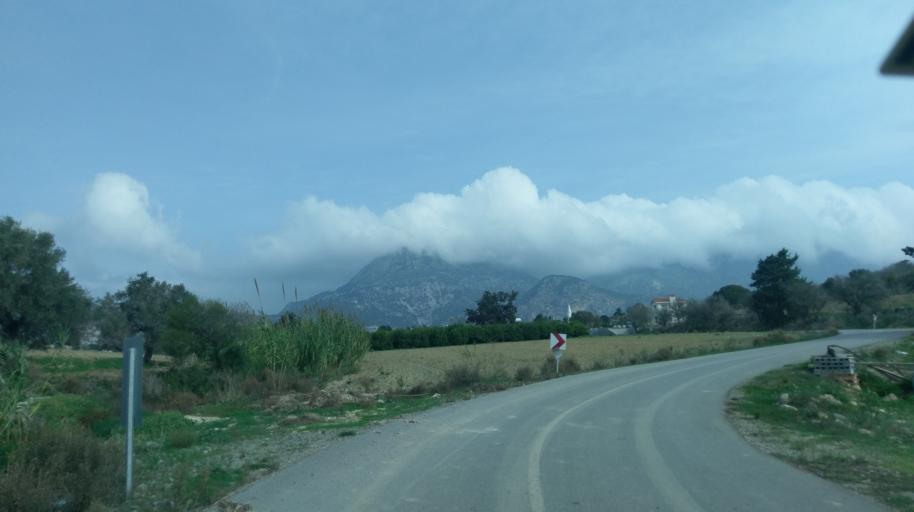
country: CY
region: Keryneia
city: Lapithos
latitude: 35.2984
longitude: 33.1044
